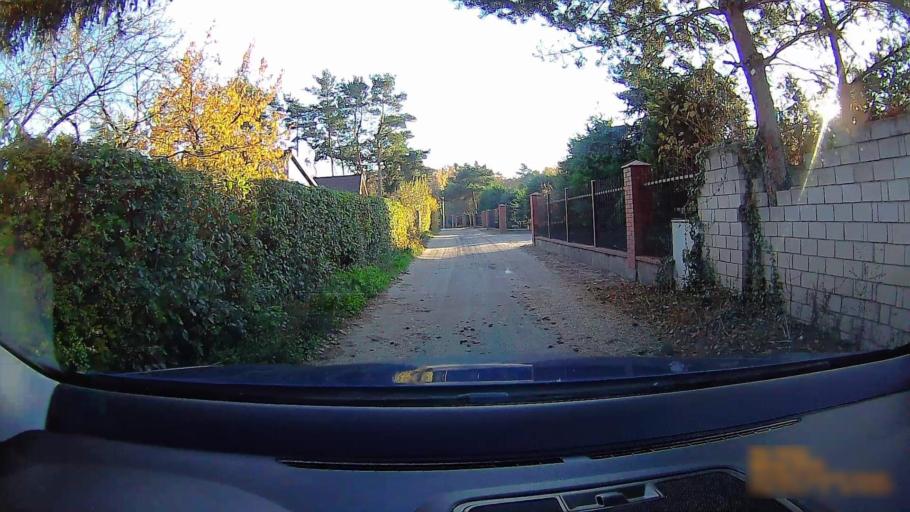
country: PL
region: Greater Poland Voivodeship
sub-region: Powiat koninski
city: Stare Miasto
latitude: 52.2036
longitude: 18.2051
